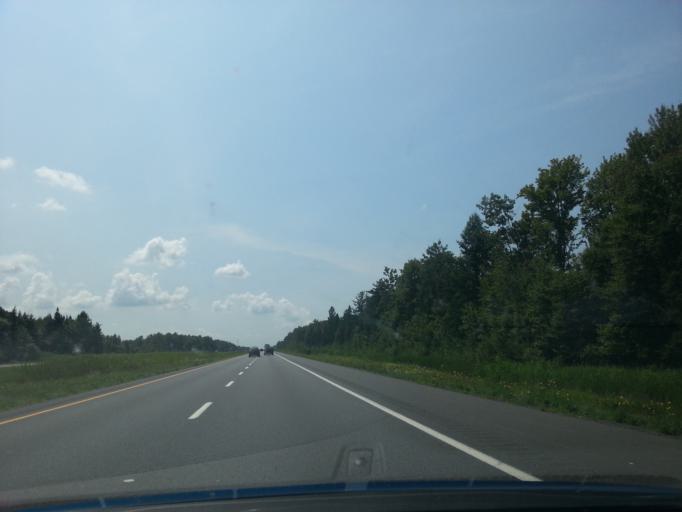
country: CA
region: Quebec
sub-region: Mauricie
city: Daveluyville
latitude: 46.2067
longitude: -72.0736
